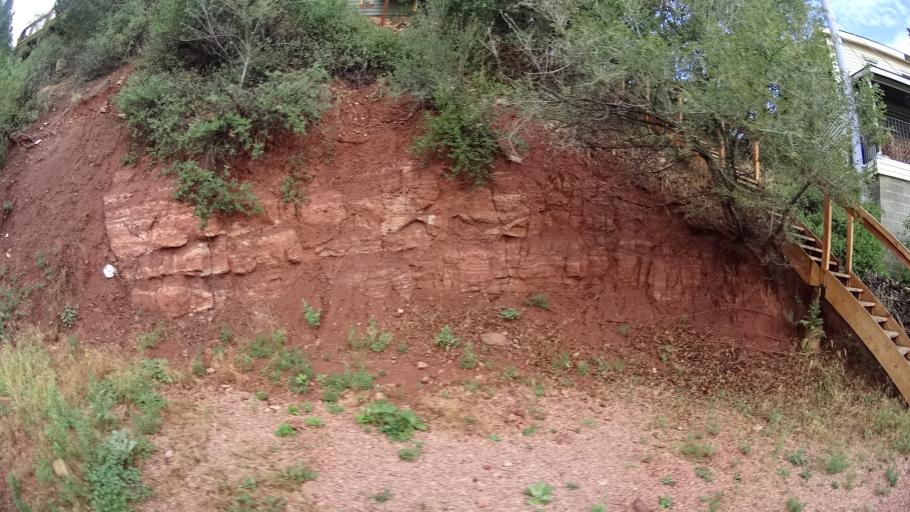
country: US
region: Colorado
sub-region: El Paso County
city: Manitou Springs
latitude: 38.8544
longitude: -104.9103
